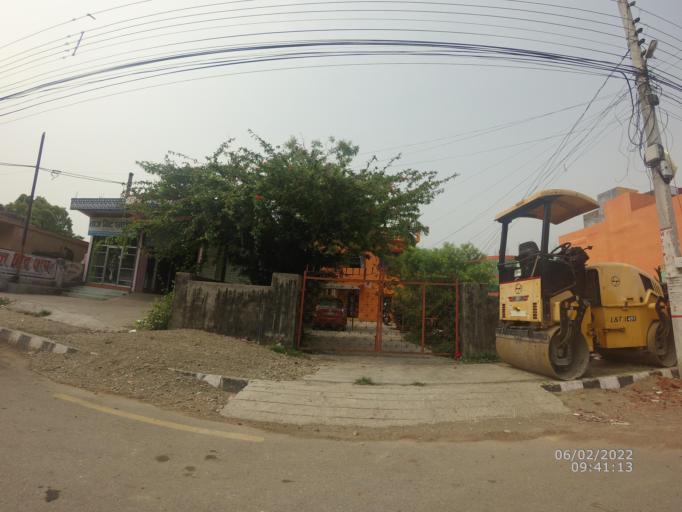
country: NP
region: Western Region
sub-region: Lumbini Zone
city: Bhairahawa
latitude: 27.5021
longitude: 83.4541
